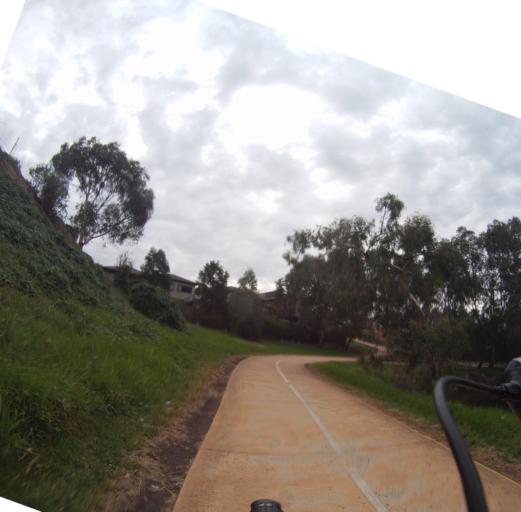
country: AU
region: Victoria
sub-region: Moreland
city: Coburg North
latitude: -37.7292
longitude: 144.9663
